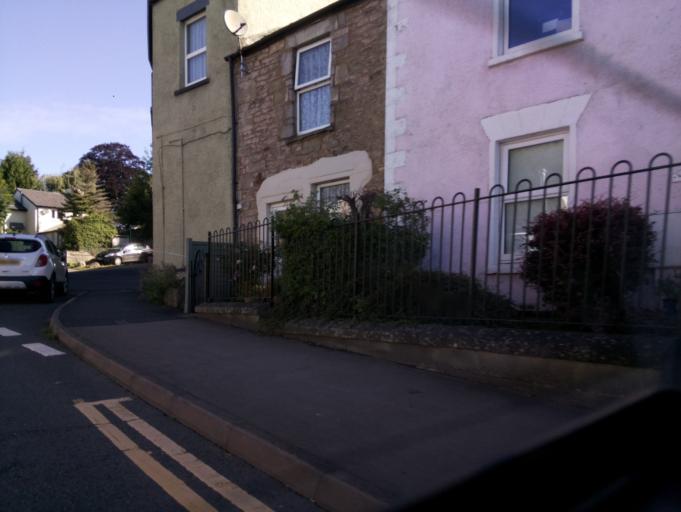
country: GB
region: England
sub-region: Gloucestershire
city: Coleford
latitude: 51.7949
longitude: -2.6181
